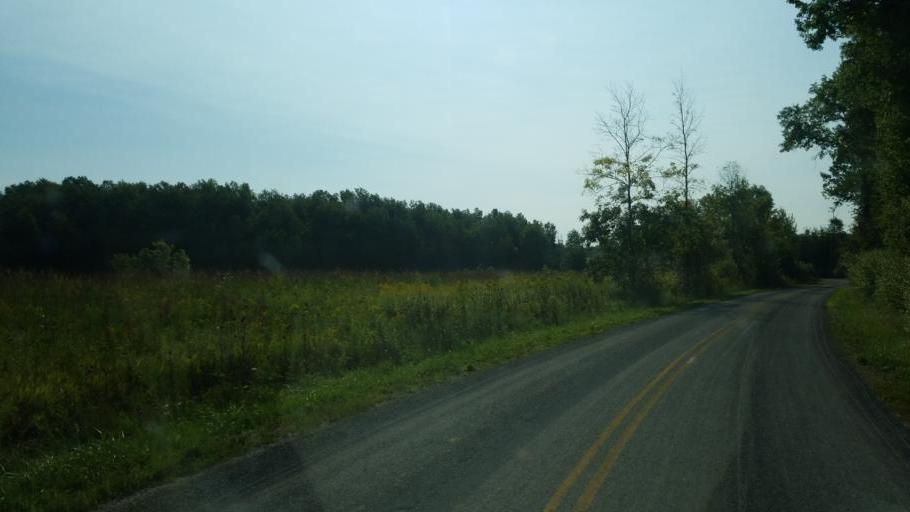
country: US
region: Ohio
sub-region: Ashtabula County
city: Orwell
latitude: 41.4769
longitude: -80.9171
